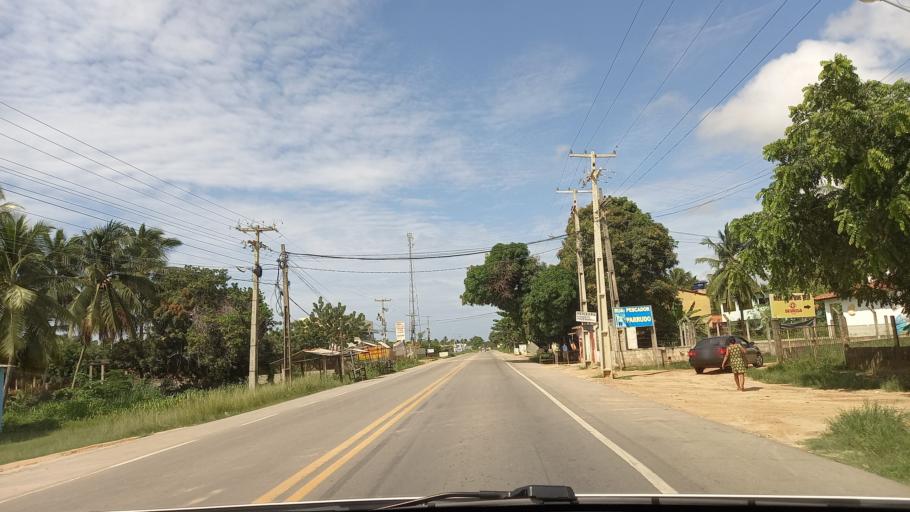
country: BR
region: Pernambuco
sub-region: Sao Jose Da Coroa Grande
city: Sao Jose da Coroa Grande
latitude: -8.9529
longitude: -35.1772
